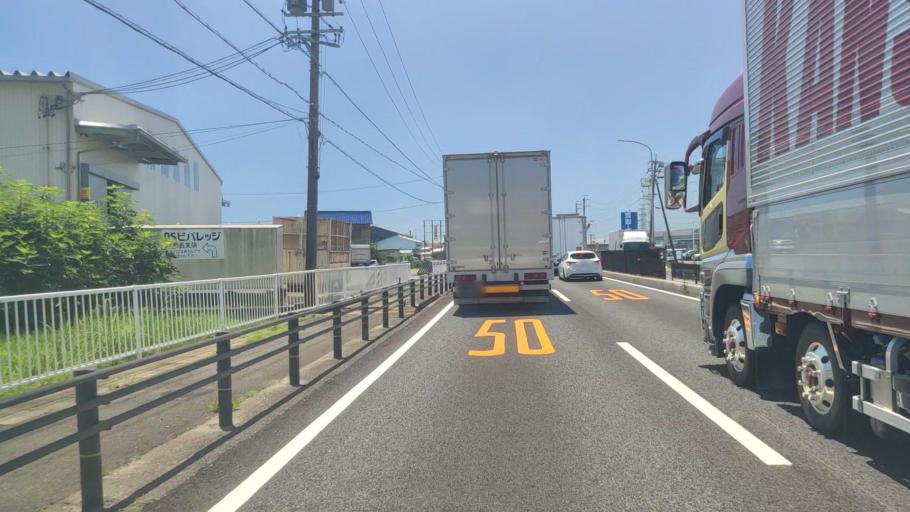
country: JP
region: Mie
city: Yokkaichi
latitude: 35.0415
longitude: 136.6923
